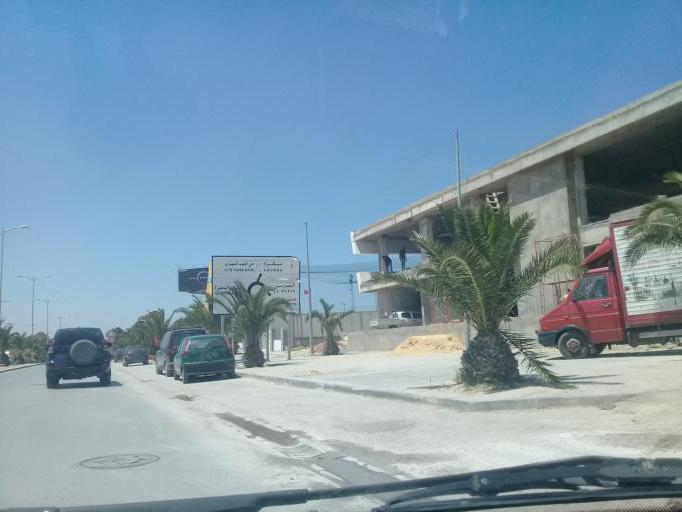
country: TN
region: Tunis
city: La Goulette
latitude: 36.8451
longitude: 10.2613
